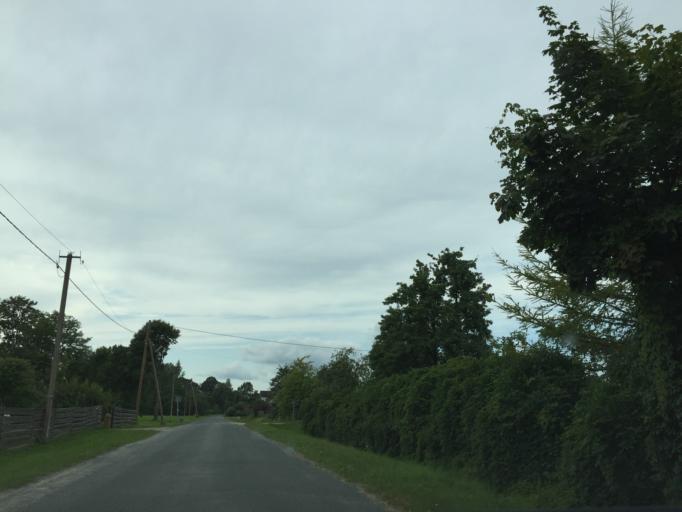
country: LV
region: Ogre
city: Ogre
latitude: 56.7676
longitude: 24.6548
